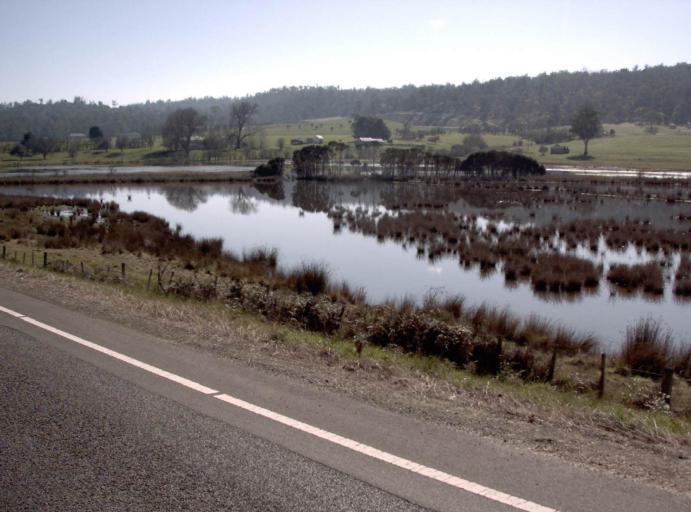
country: AU
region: Tasmania
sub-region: Launceston
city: Mayfield
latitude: -41.3188
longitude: 147.0581
